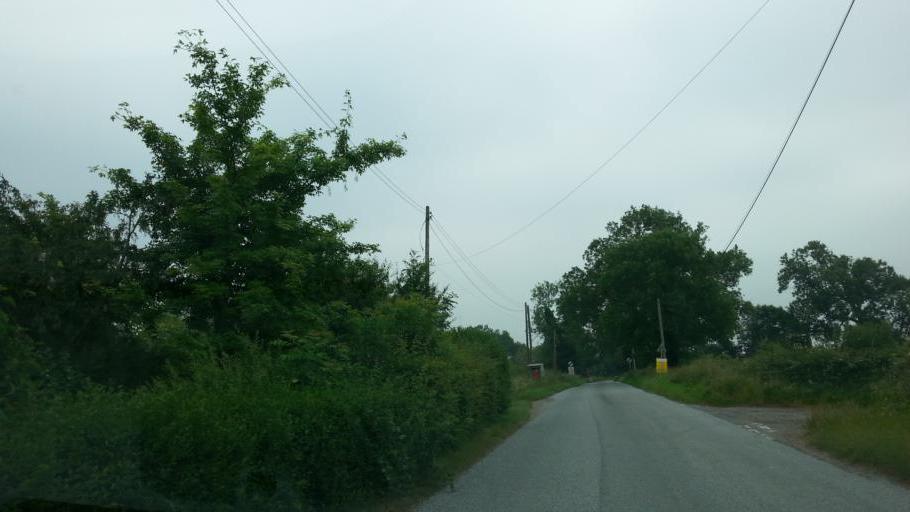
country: GB
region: England
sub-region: Staffordshire
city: Colwich
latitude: 52.8322
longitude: -1.9599
